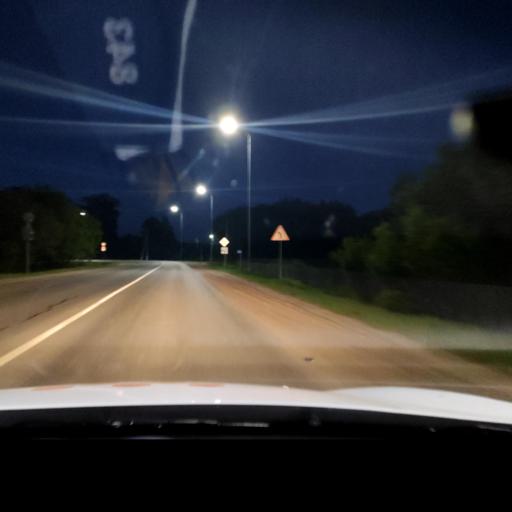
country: RU
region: Tatarstan
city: Rybnaya Sloboda
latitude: 55.4715
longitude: 50.0220
